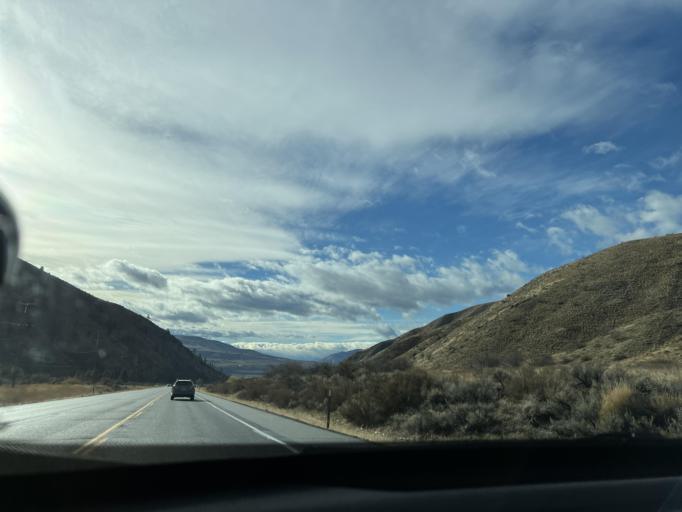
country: US
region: Washington
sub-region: Chelan County
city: Manson
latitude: 47.7965
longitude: -120.1332
